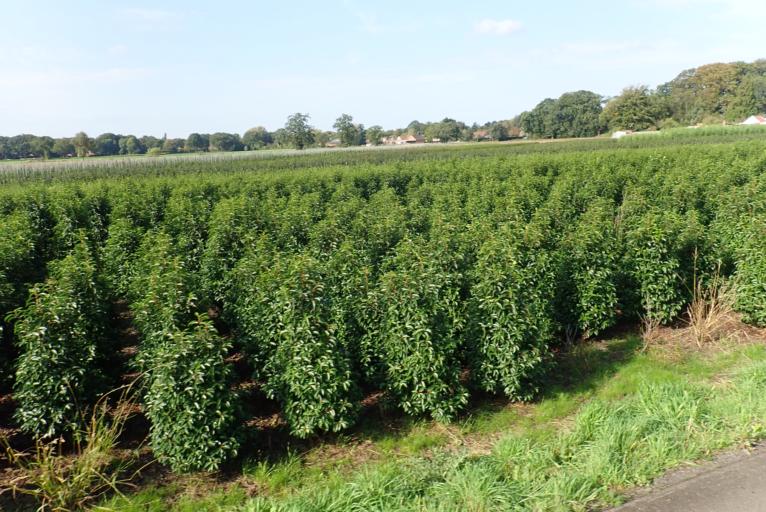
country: BE
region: Flanders
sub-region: Provincie Antwerpen
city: Kalmthout
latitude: 51.3865
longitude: 4.4668
